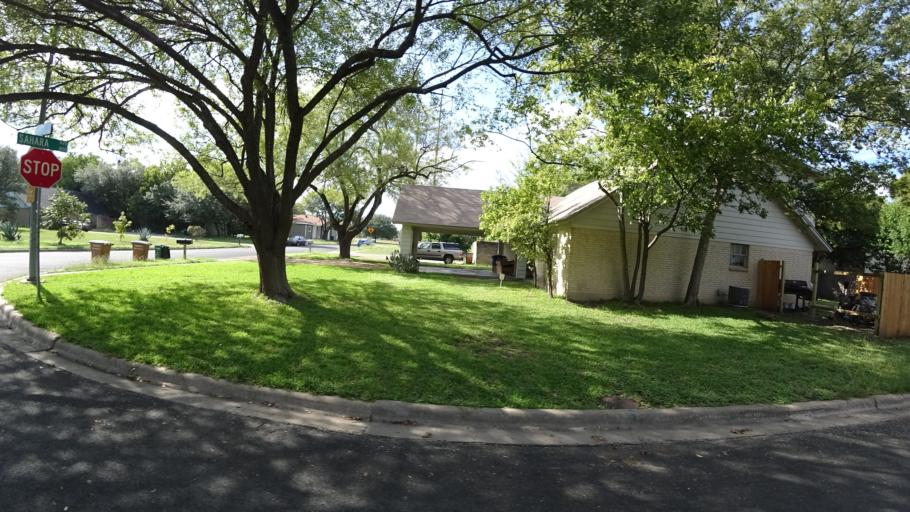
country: US
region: Texas
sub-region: Travis County
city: Onion Creek
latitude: 30.2054
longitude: -97.7862
